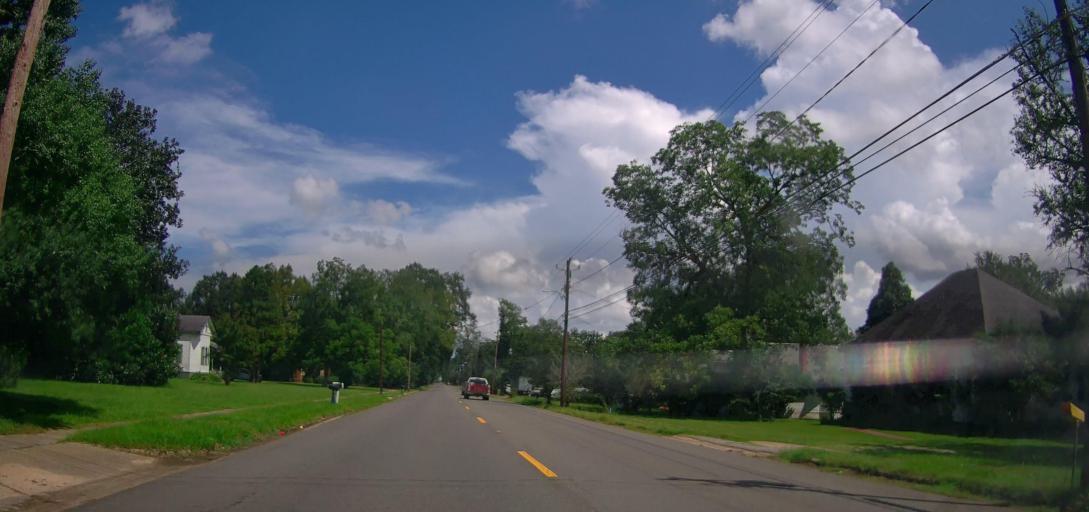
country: US
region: Georgia
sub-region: Macon County
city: Marshallville
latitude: 32.4564
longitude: -83.9485
